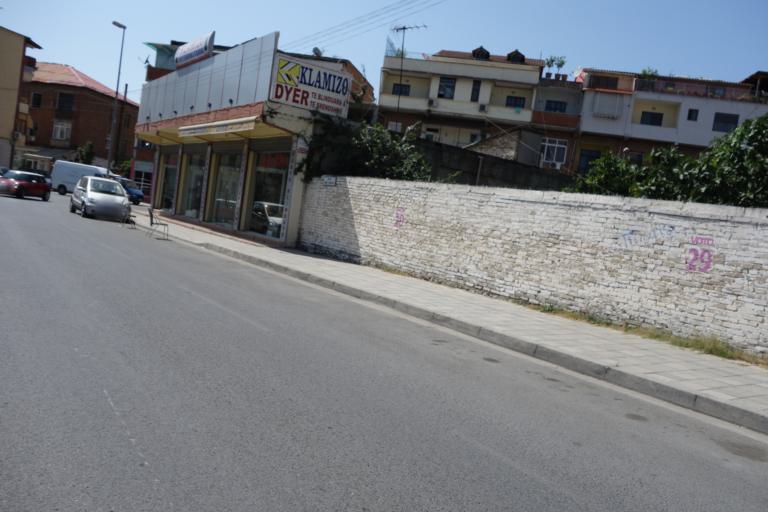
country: AL
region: Tirane
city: Tirana
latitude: 41.3198
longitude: 19.8092
